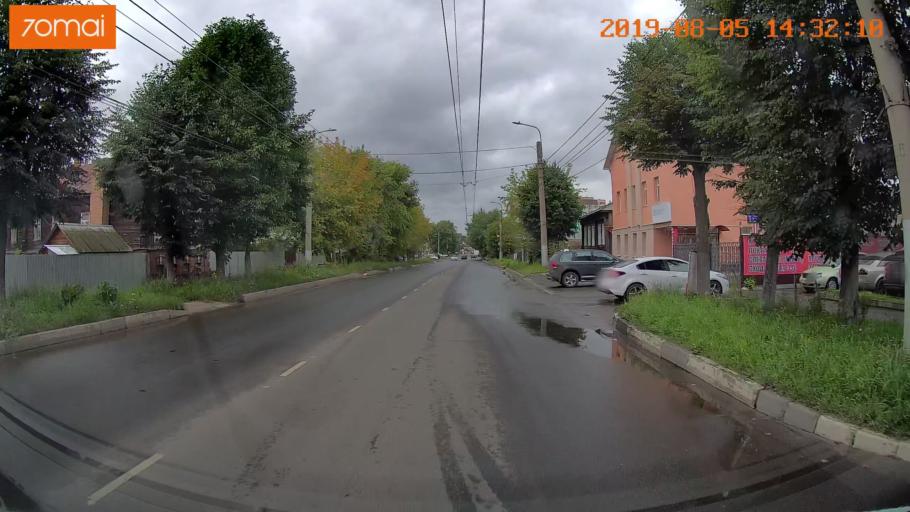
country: RU
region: Ivanovo
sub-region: Gorod Ivanovo
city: Ivanovo
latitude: 56.9901
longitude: 40.9927
